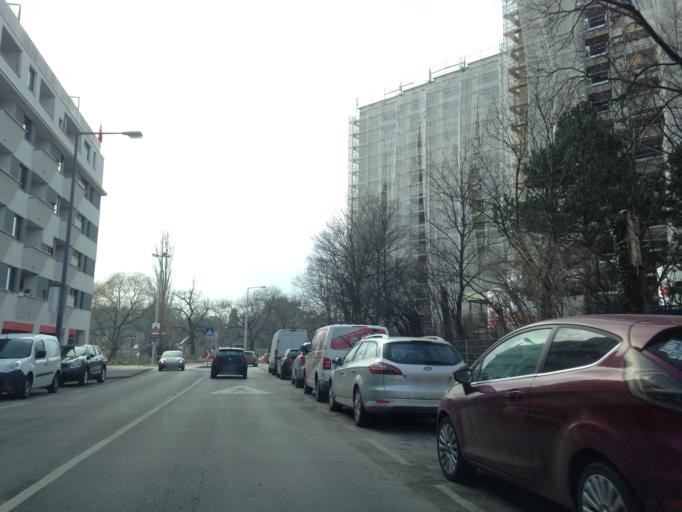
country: AT
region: Vienna
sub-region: Wien Stadt
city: Vienna
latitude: 48.1971
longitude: 16.3019
